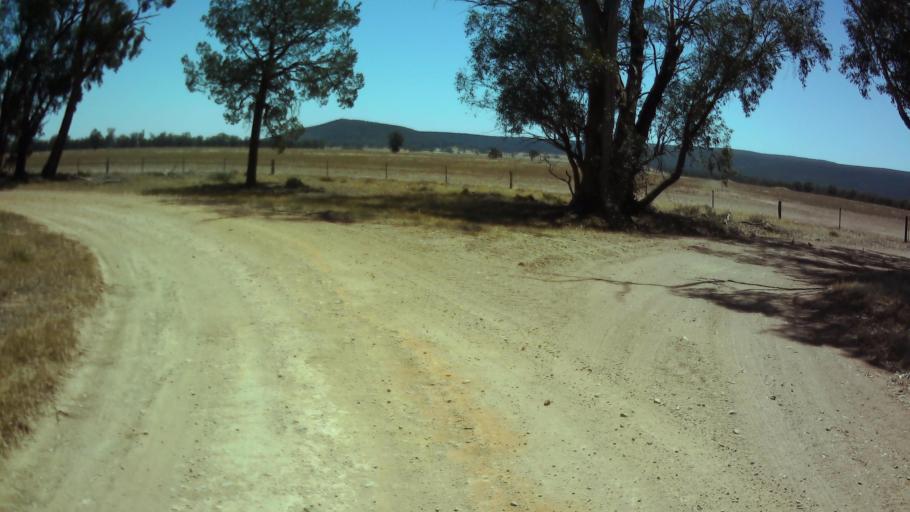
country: AU
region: New South Wales
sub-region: Weddin
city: Grenfell
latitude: -34.0085
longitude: 147.9642
